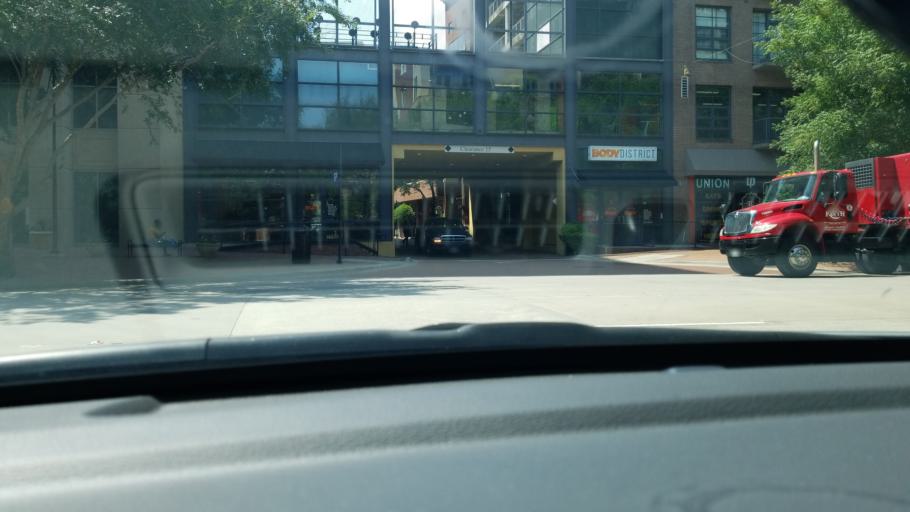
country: US
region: Texas
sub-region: Dallas County
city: Addison
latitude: 32.9623
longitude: -96.8227
